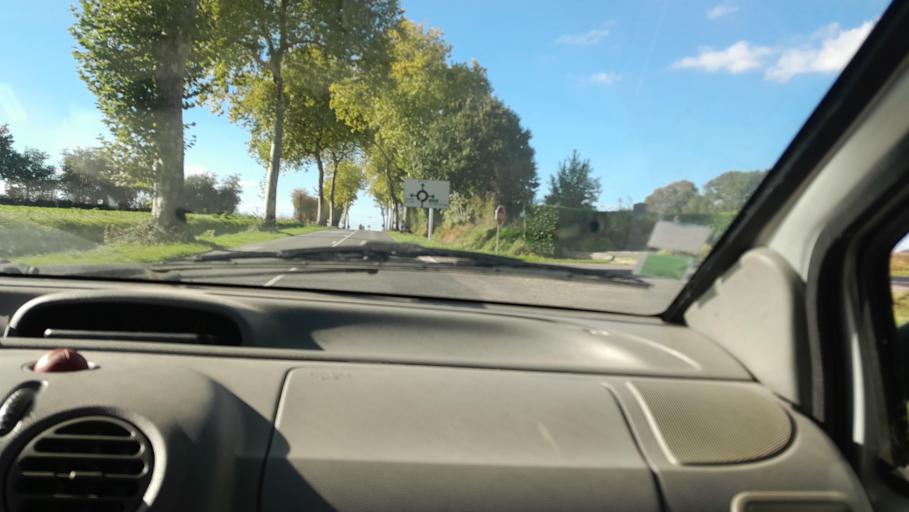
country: FR
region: Pays de la Loire
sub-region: Departement de la Mayenne
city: Cosse-le-Vivien
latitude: 47.9505
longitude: -0.9246
